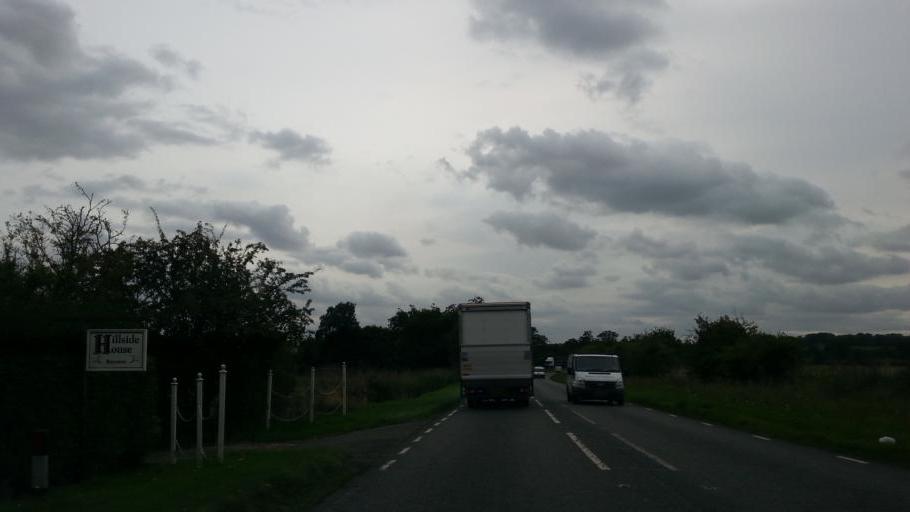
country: GB
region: England
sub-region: Cambridgeshire
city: Melbourn
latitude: 52.0524
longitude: 0.0195
